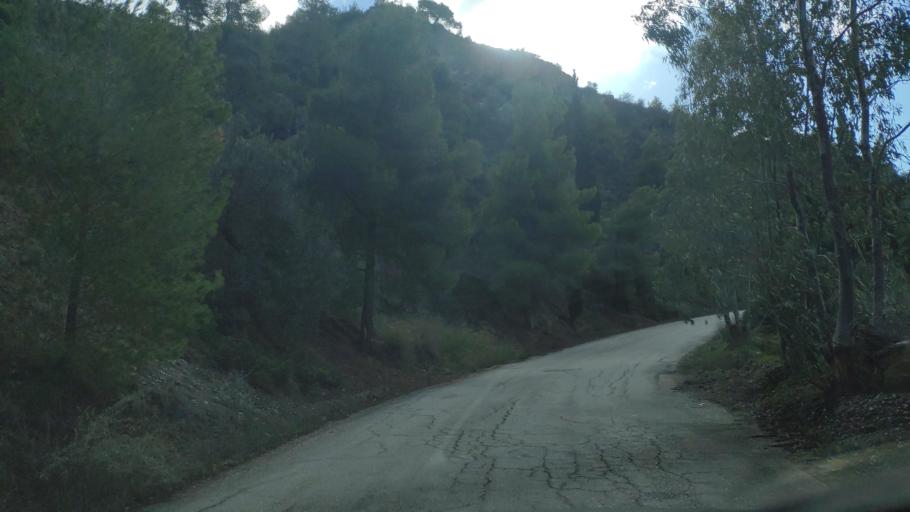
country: GR
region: West Greece
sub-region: Nomos Achaias
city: Aiyira
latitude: 38.1243
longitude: 22.4356
